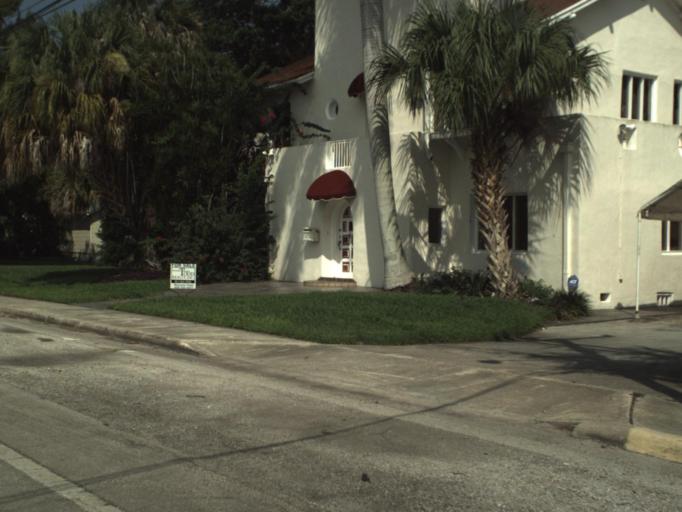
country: US
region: Florida
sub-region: Palm Beach County
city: Pahokee
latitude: 26.8142
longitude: -80.6825
